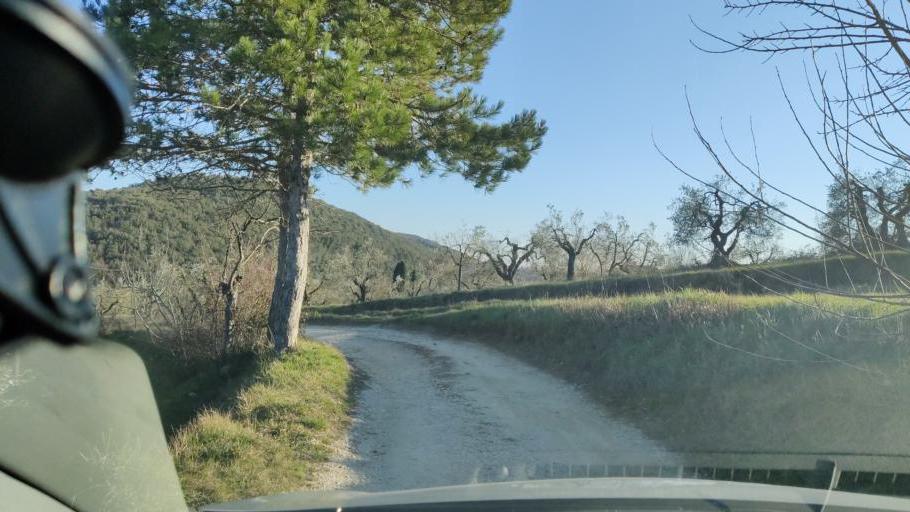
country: IT
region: Umbria
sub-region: Provincia di Terni
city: Fornole
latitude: 42.5590
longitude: 12.4497
